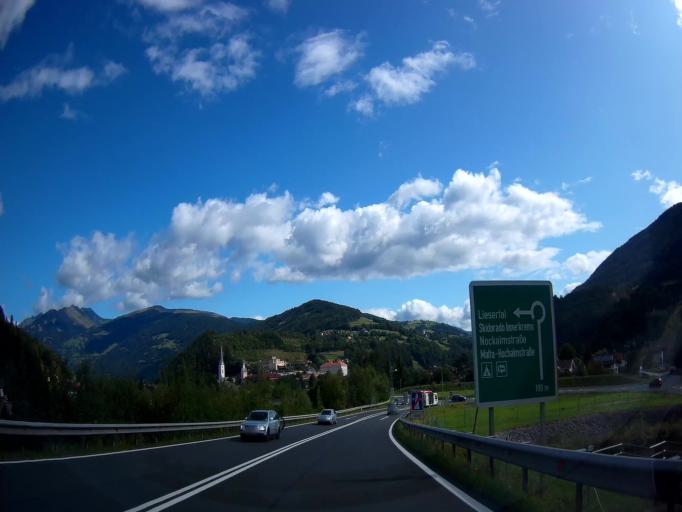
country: AT
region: Carinthia
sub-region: Politischer Bezirk Spittal an der Drau
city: Gmuend
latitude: 46.9007
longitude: 13.5320
